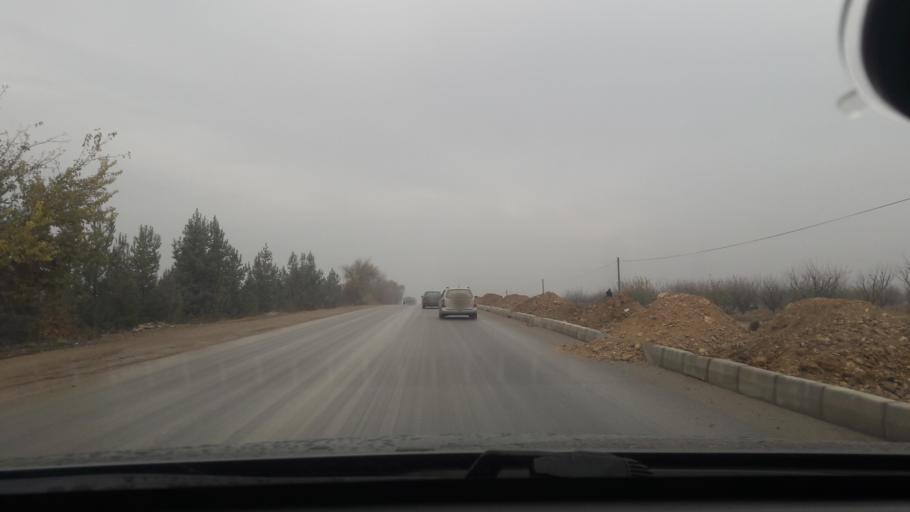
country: TJ
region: Khatlon
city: Obikiik
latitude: 38.2900
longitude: 68.6861
